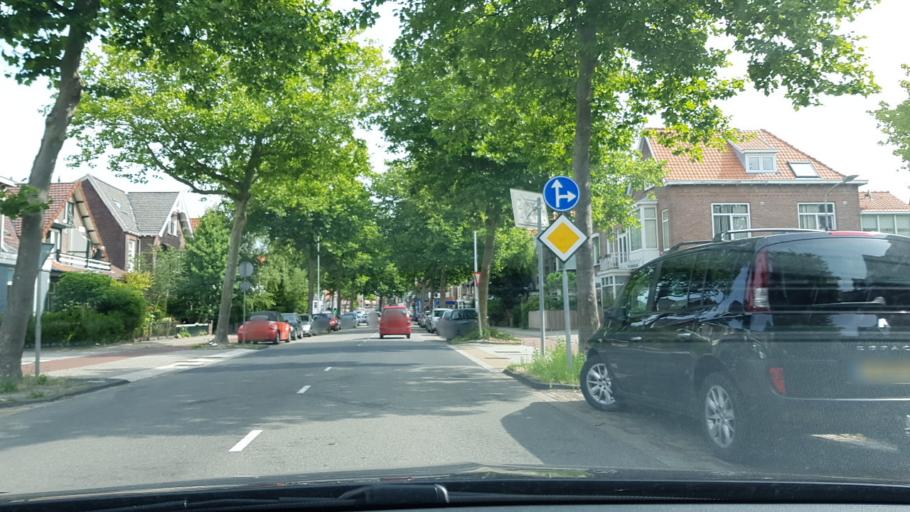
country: NL
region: North Holland
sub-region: Gemeente Haarlem
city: Haarlem
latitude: 52.4027
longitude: 4.6466
